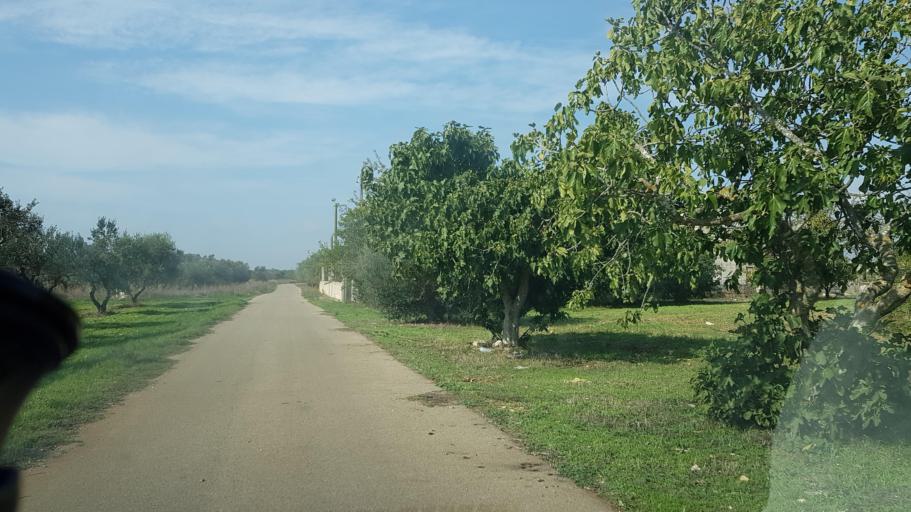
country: IT
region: Apulia
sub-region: Provincia di Brindisi
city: San Pancrazio Salentino
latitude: 40.4413
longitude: 17.8455
